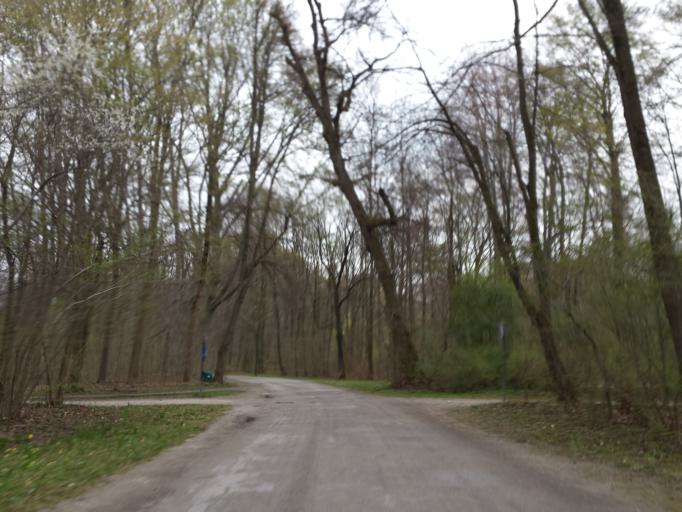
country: DE
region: Bavaria
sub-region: Upper Bavaria
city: Bogenhausen
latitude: 48.1763
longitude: 11.6158
